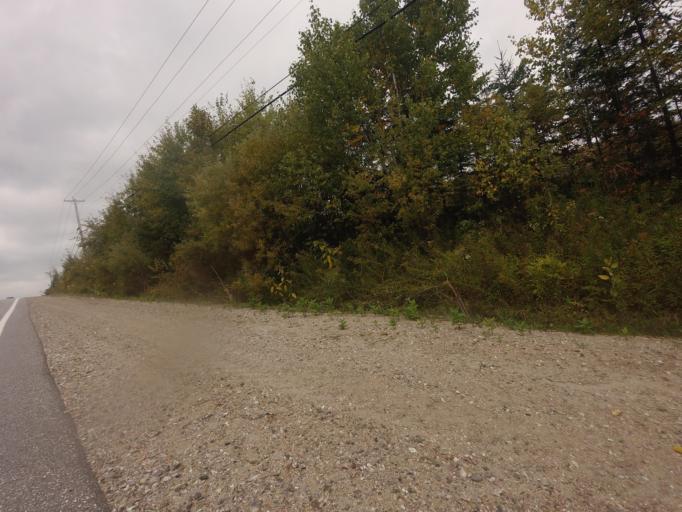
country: CA
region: Quebec
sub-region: Outaouais
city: Wakefield
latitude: 45.9347
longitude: -75.9970
